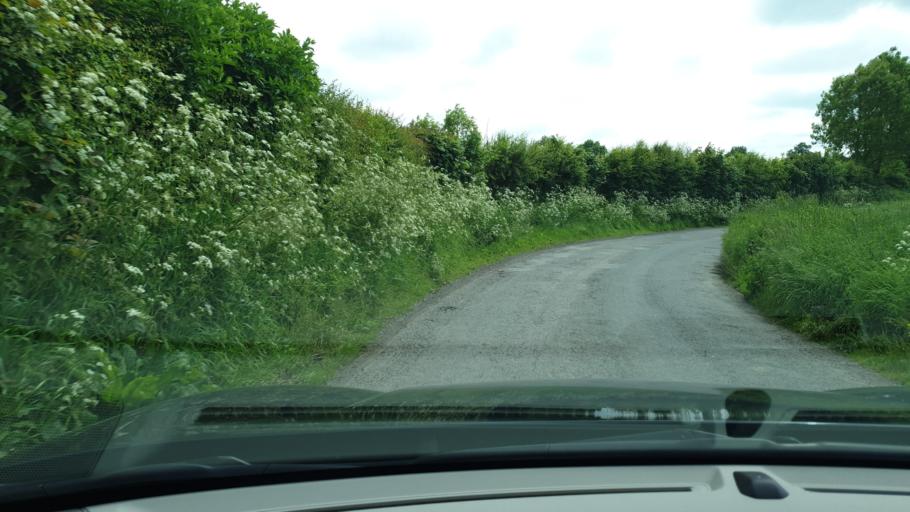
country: IE
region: Ulster
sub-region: An Cabhan
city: Kingscourt
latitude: 53.7997
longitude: -6.7209
